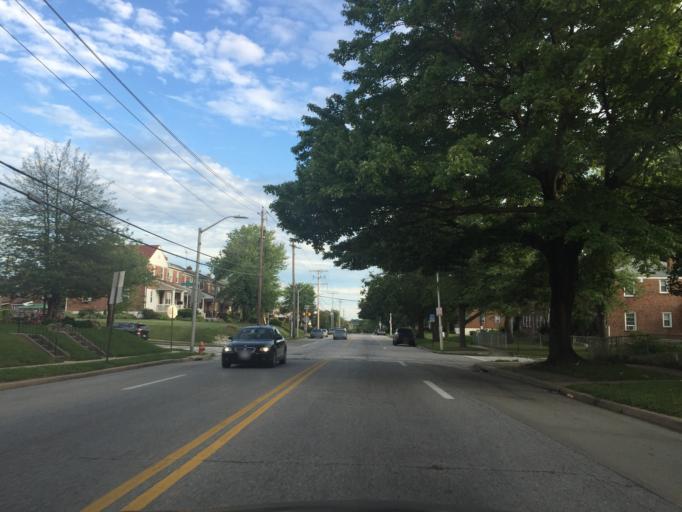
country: US
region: Maryland
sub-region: Baltimore County
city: Towson
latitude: 39.3647
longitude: -76.5938
